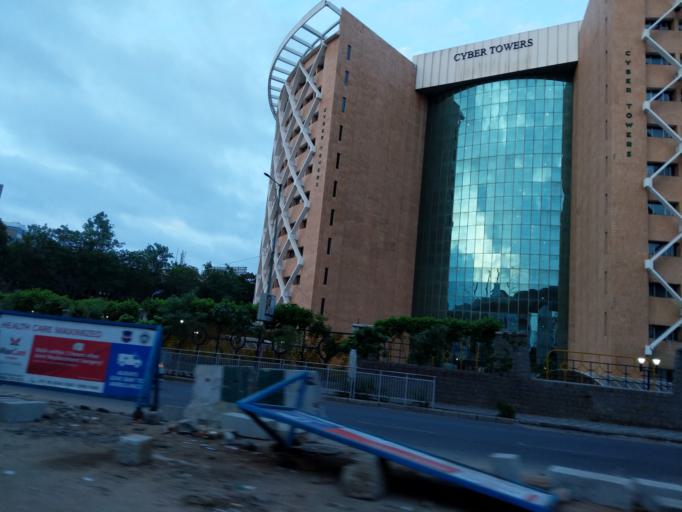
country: IN
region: Telangana
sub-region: Rangareddi
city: Kukatpalli
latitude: 17.4510
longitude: 78.3817
